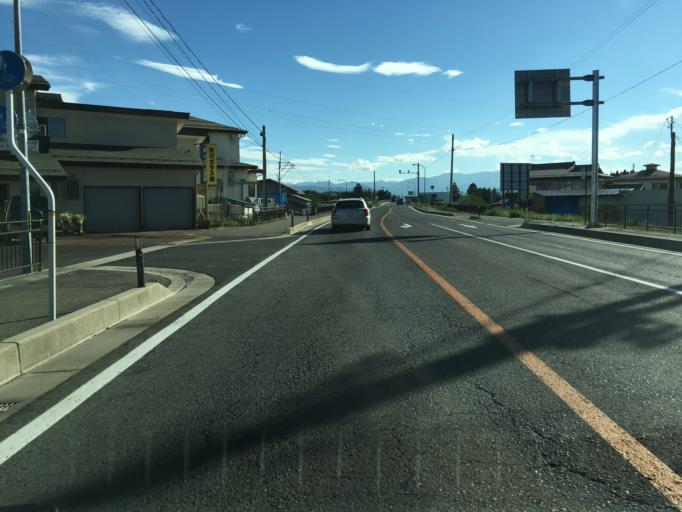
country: JP
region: Yamagata
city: Takahata
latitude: 37.9890
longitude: 140.1430
